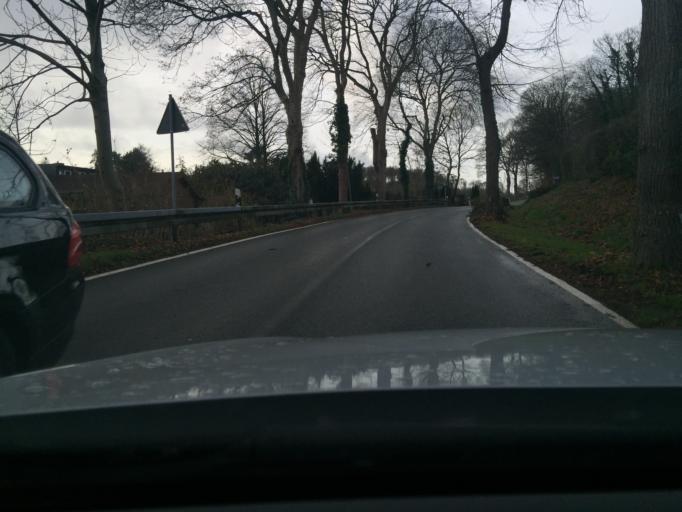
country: DE
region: North Rhine-Westphalia
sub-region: Regierungsbezirk Dusseldorf
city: Velbert
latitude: 51.3802
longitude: 7.0762
